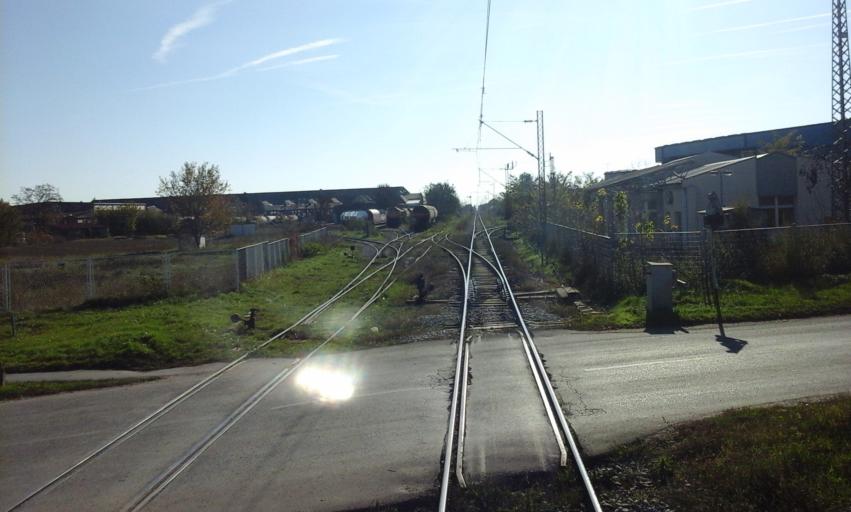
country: RS
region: Autonomna Pokrajina Vojvodina
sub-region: Severnobacki Okrug
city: Subotica
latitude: 46.0662
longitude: 19.6878
